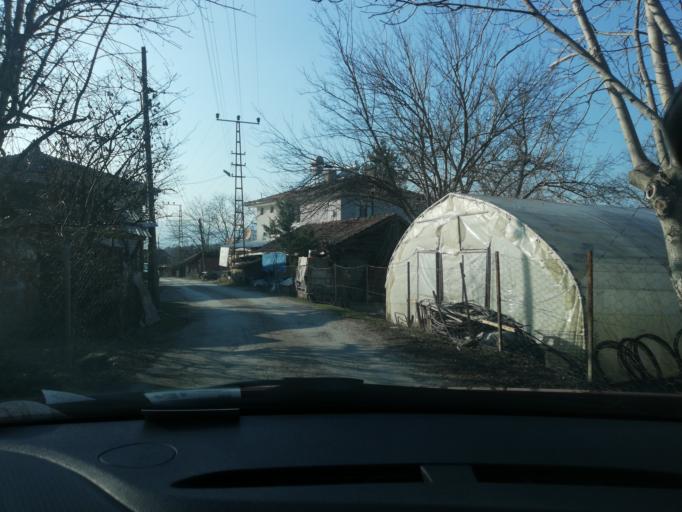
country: TR
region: Karabuk
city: Safranbolu
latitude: 41.2162
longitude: 32.7446
